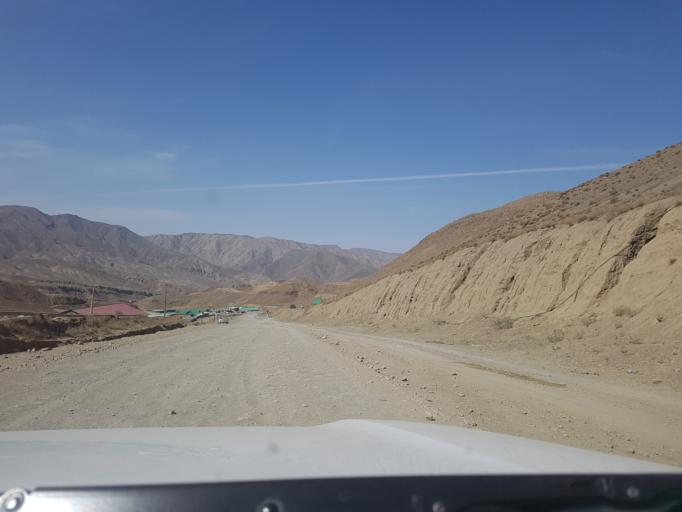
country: TM
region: Ahal
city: Baharly
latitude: 38.4497
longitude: 57.0473
